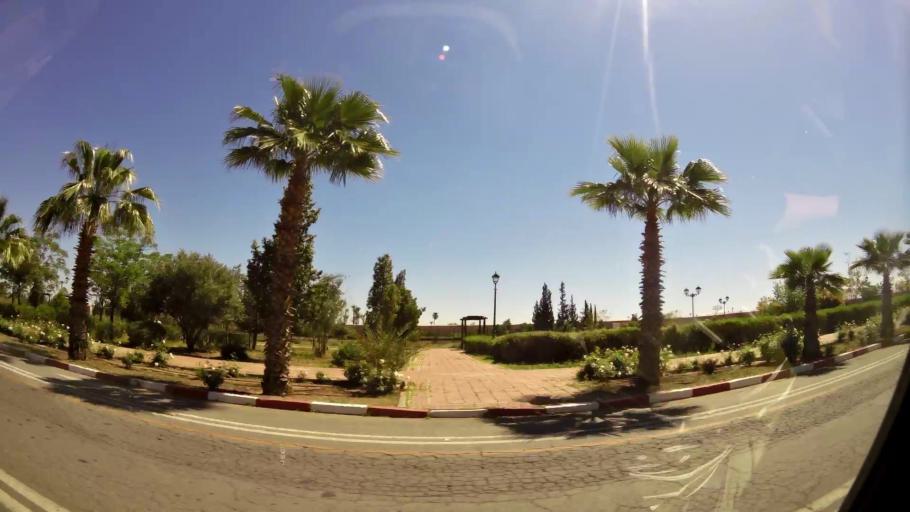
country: MA
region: Marrakech-Tensift-Al Haouz
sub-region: Marrakech
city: Marrakesh
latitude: 31.5942
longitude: -7.9860
